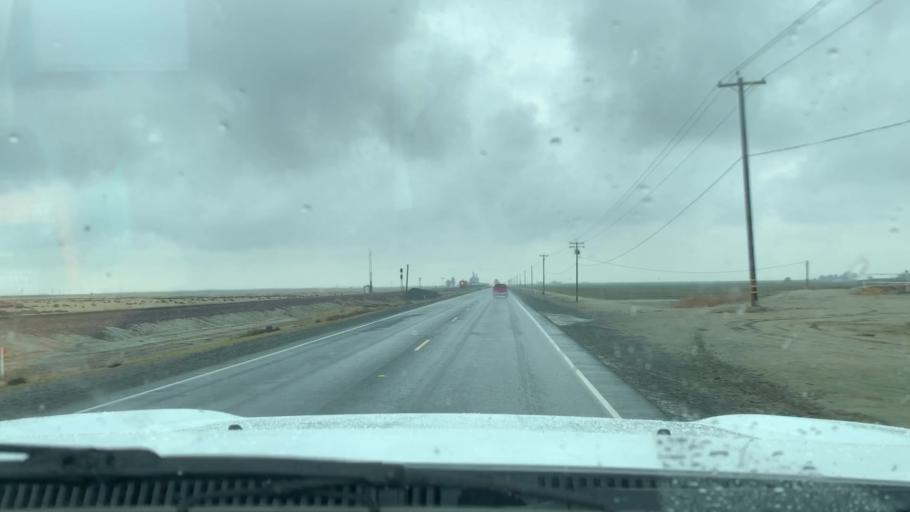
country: US
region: California
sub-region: Tulare County
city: Alpaugh
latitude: 35.9738
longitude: -119.4655
